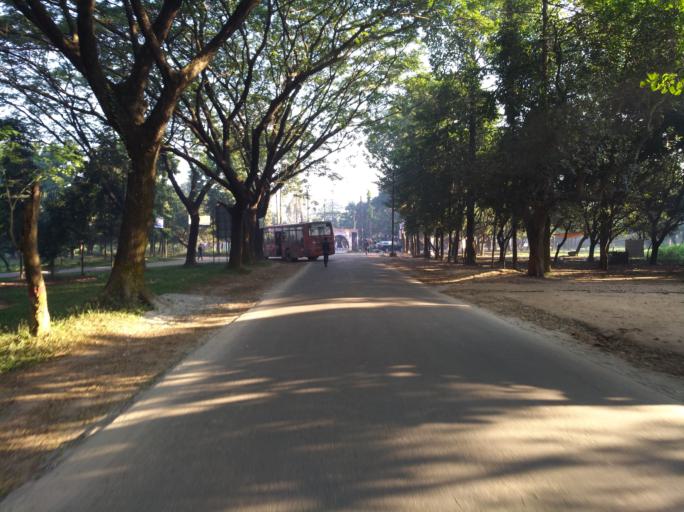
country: BD
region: Dhaka
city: Tungi
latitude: 23.8893
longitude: 90.2710
